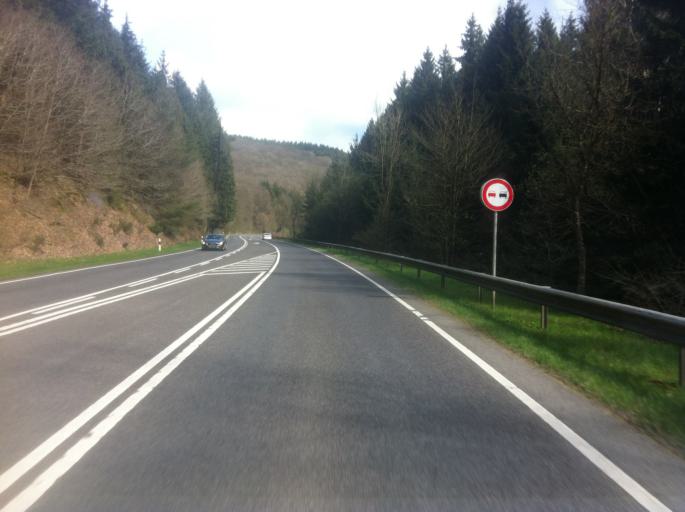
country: LU
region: Diekirch
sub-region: Canton de Wiltz
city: Winseler
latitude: 49.9434
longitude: 5.9011
